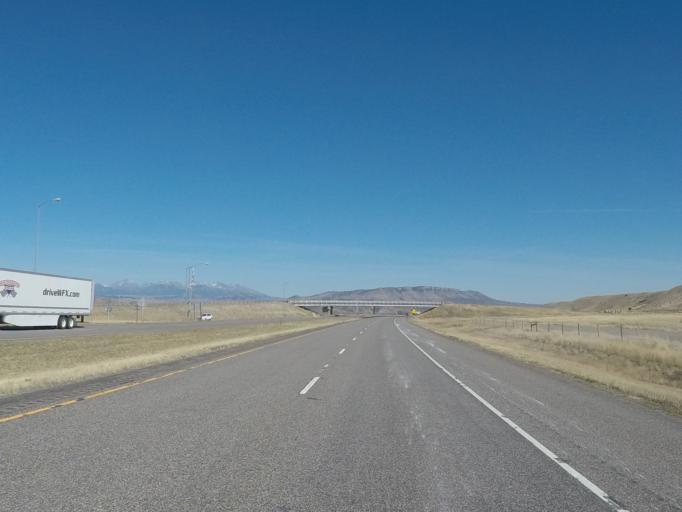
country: US
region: Montana
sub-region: Park County
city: Livingston
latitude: 45.6862
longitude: -110.5029
